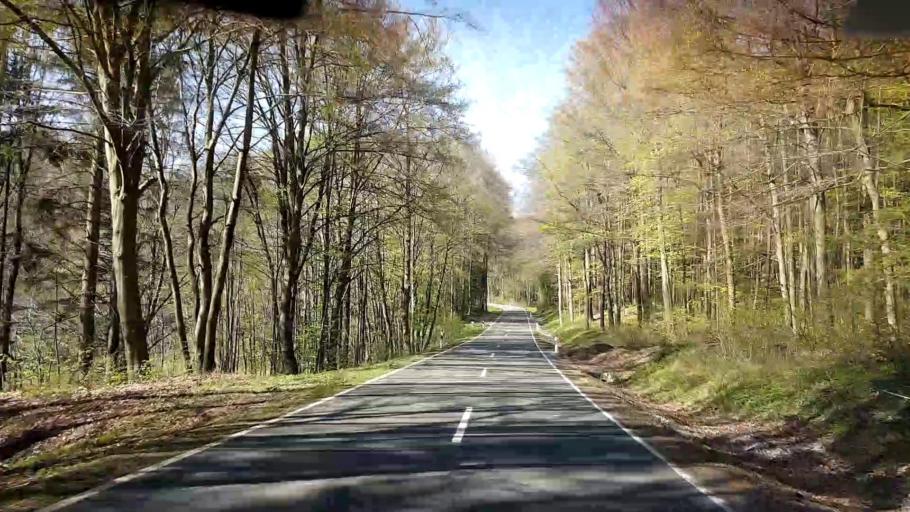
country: DE
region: Bavaria
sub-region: Upper Franconia
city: Pottenstein
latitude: 49.7943
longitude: 11.4086
